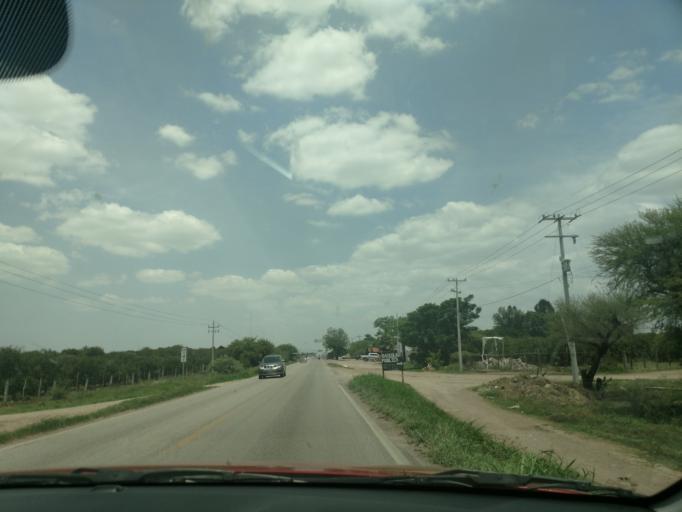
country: MX
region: San Luis Potosi
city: Ciudad Fernandez
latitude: 21.9482
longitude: -100.0578
